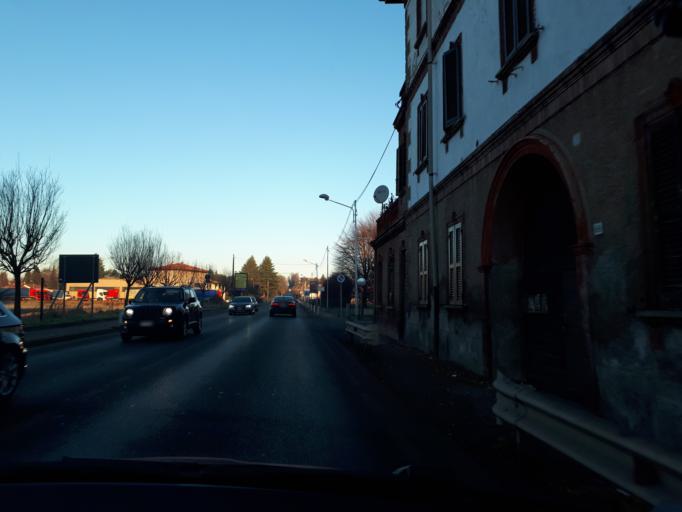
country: IT
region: Lombardy
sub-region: Provincia di Como
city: Cermenate
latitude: 45.7048
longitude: 9.0905
